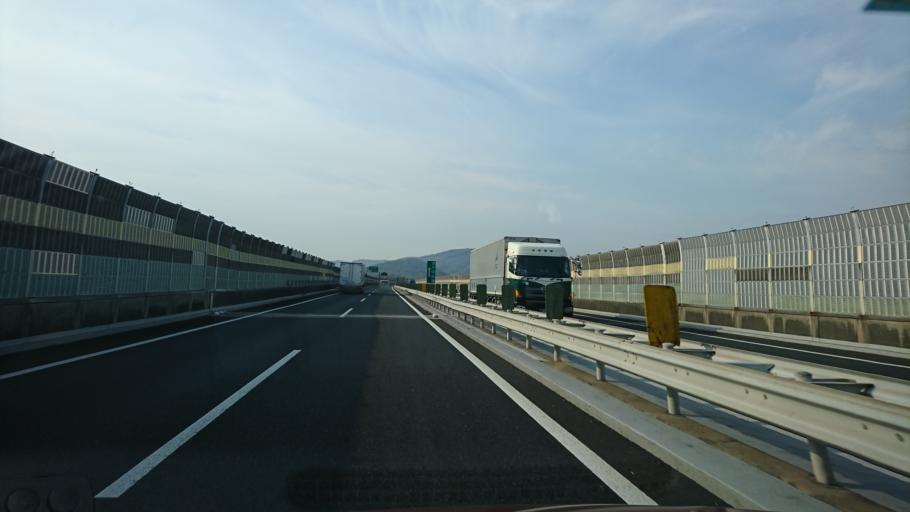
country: JP
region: Okayama
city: Okayama-shi
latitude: 34.7488
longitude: 134.0319
